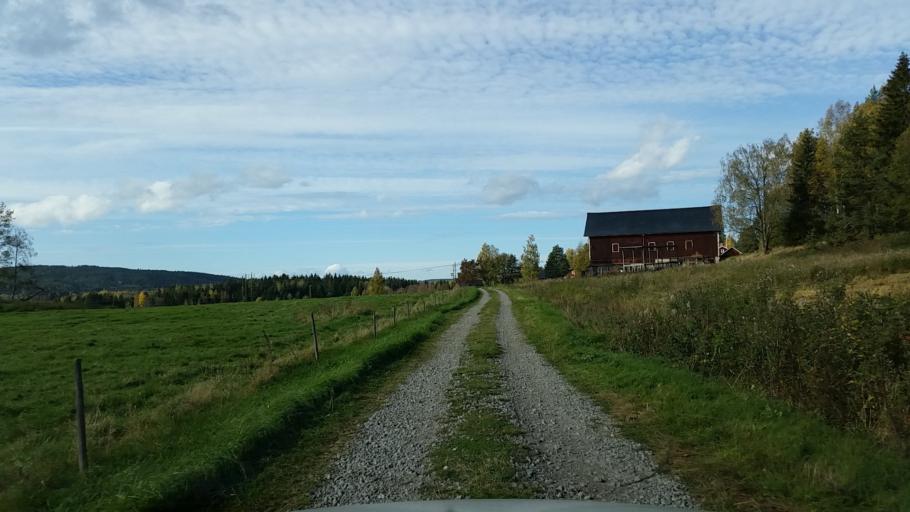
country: SE
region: Gaevleborg
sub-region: Ljusdals Kommun
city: Jaervsoe
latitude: 61.7827
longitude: 16.1693
